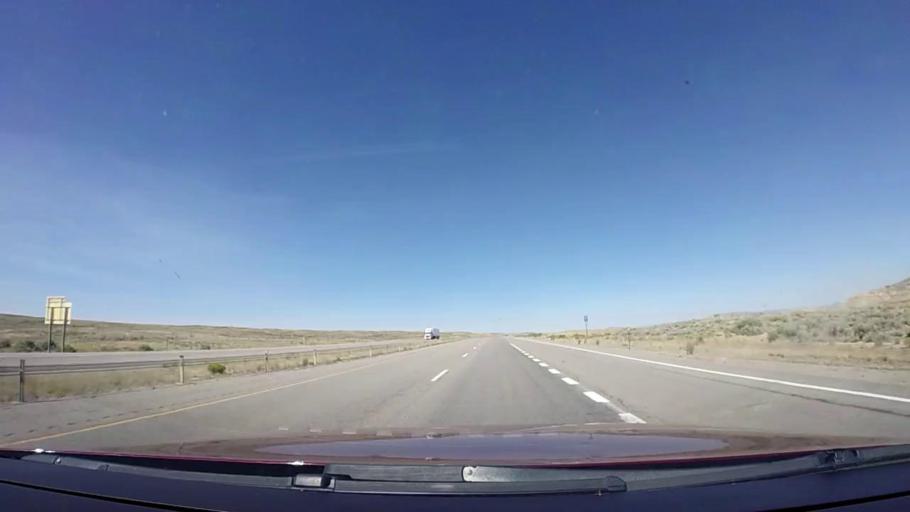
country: US
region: Wyoming
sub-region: Sweetwater County
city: Rock Springs
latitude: 41.6478
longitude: -108.6881
